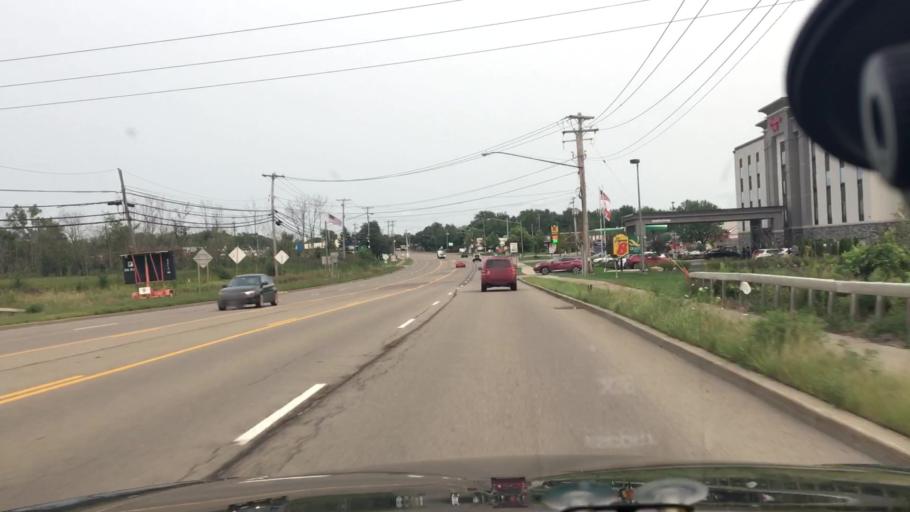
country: US
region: New York
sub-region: Erie County
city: Hamburg
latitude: 42.7399
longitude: -78.8461
